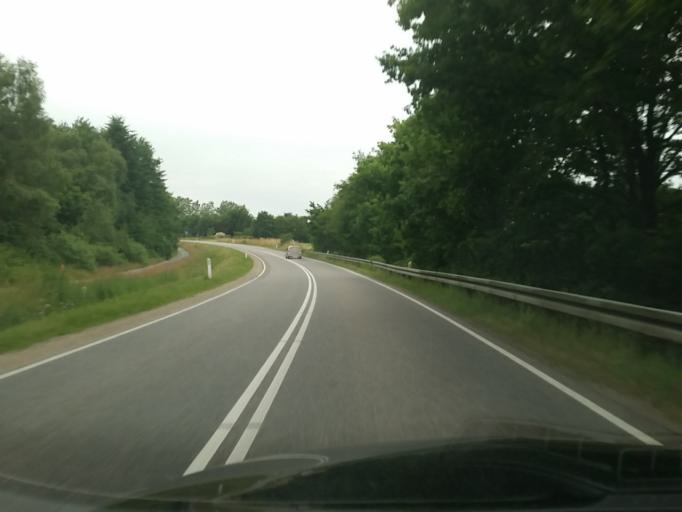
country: DK
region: South Denmark
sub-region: Billund Kommune
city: Grindsted
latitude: 55.6558
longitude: 8.8089
